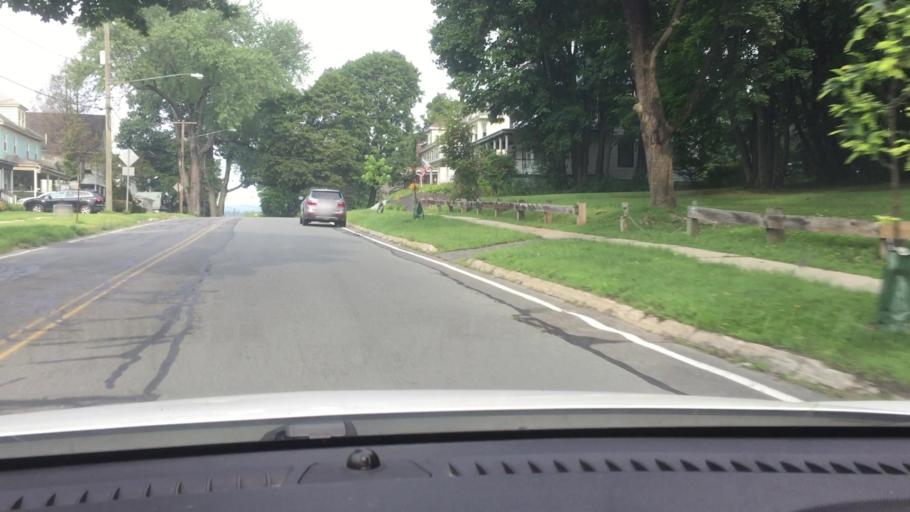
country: US
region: Massachusetts
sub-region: Berkshire County
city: Pittsfield
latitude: 42.4609
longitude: -73.2439
